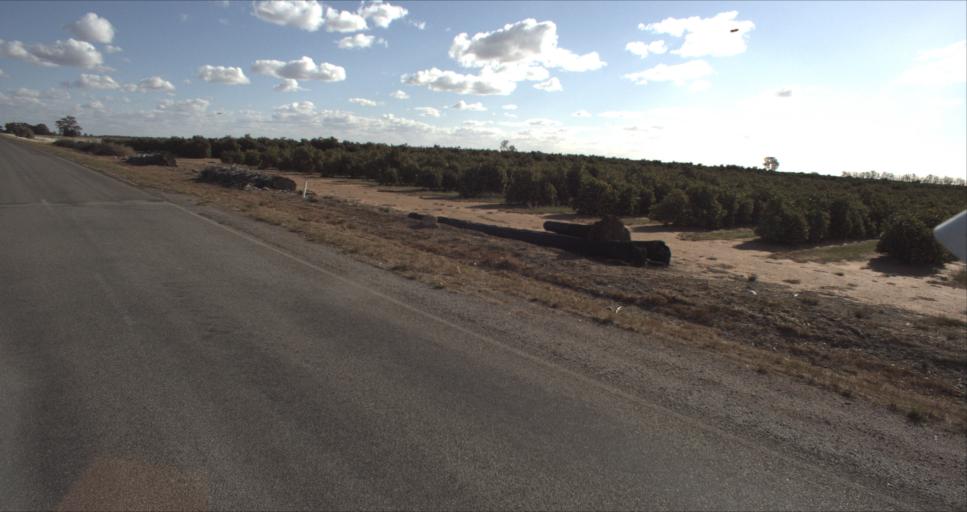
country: AU
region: New South Wales
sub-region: Leeton
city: Leeton
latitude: -34.5282
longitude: 146.2820
